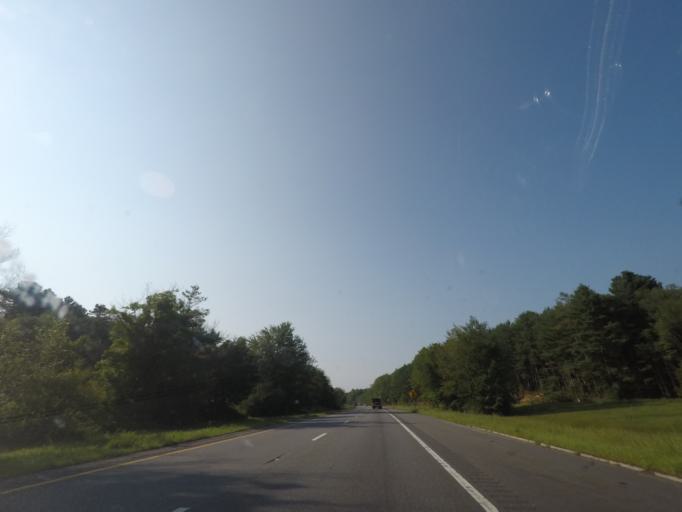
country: US
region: Massachusetts
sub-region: Worcester County
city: Webster
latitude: 42.0802
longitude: -71.8666
